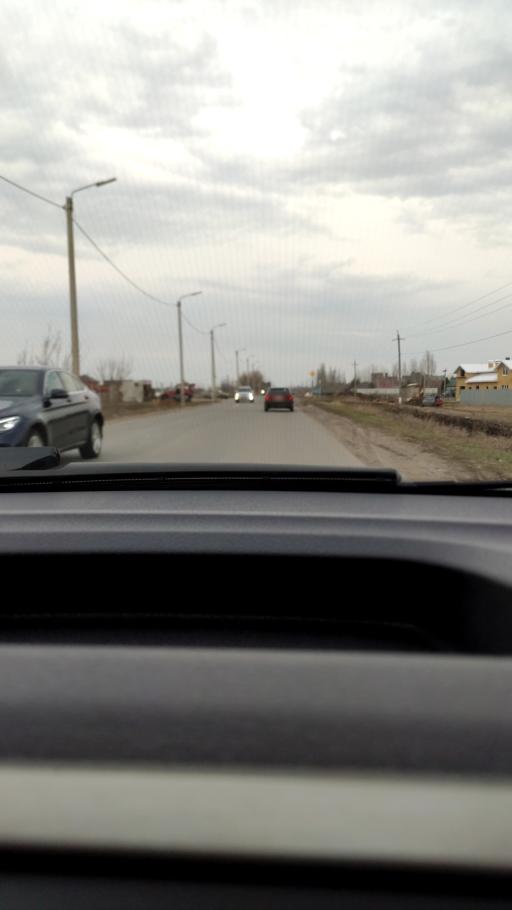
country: RU
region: Samara
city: Podstepki
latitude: 53.5230
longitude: 49.1574
